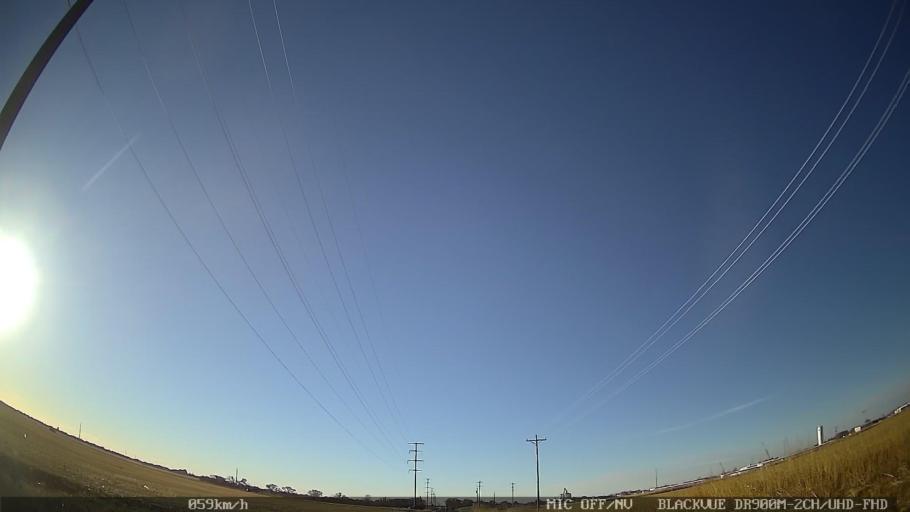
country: US
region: New Mexico
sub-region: Curry County
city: Clovis
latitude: 34.4202
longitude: -103.2493
